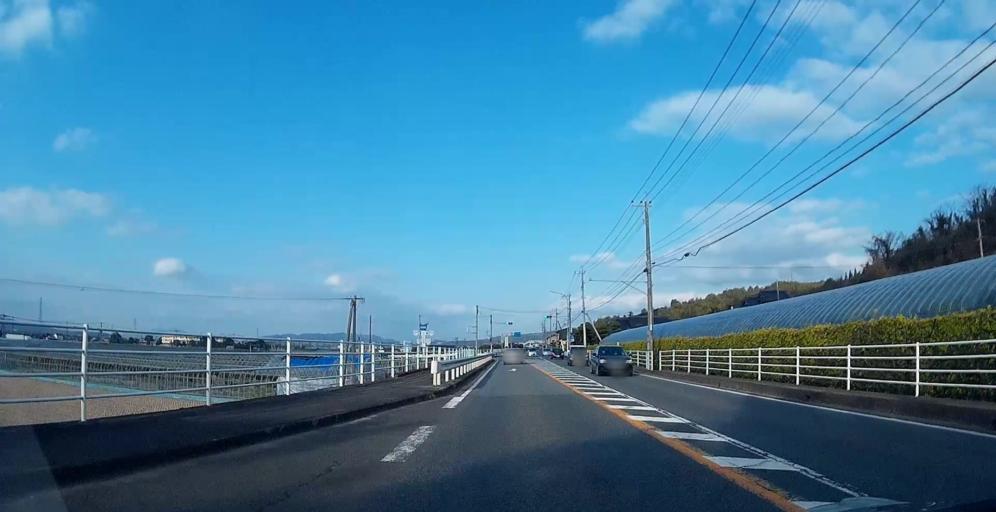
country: JP
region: Kumamoto
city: Matsubase
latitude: 32.5702
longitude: 130.6912
